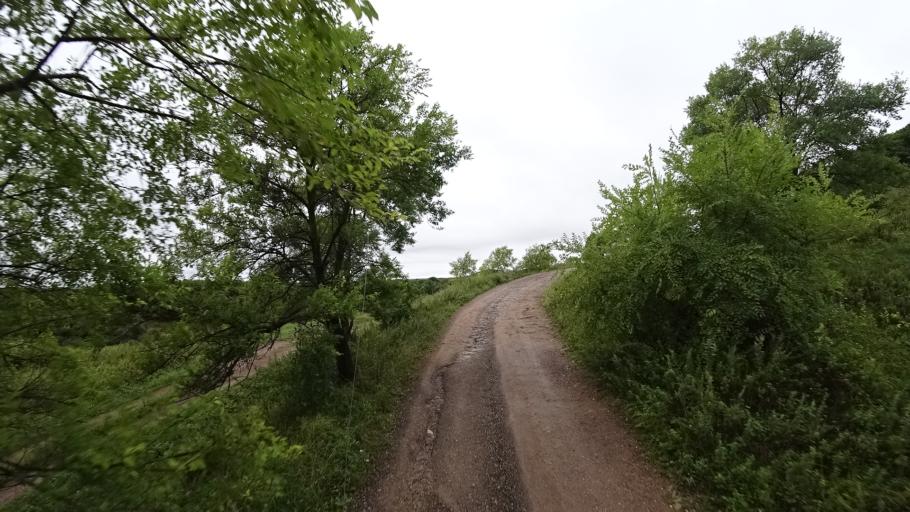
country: RU
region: Primorskiy
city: Monastyrishche
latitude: 44.2589
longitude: 132.4090
